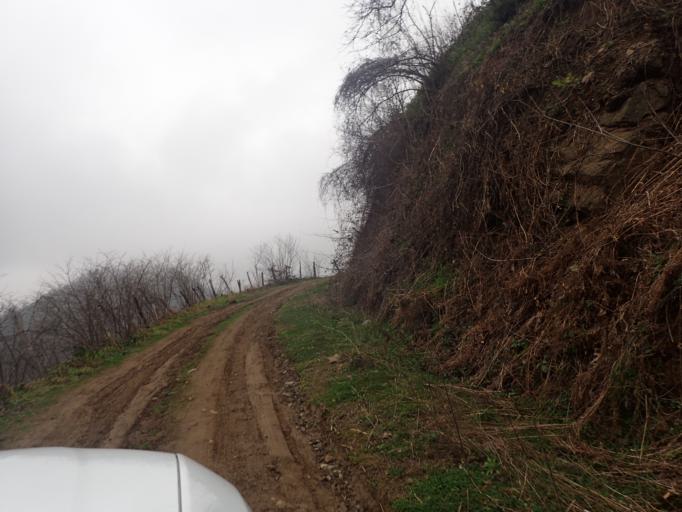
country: TR
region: Ordu
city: Camas
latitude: 40.8983
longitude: 37.5574
